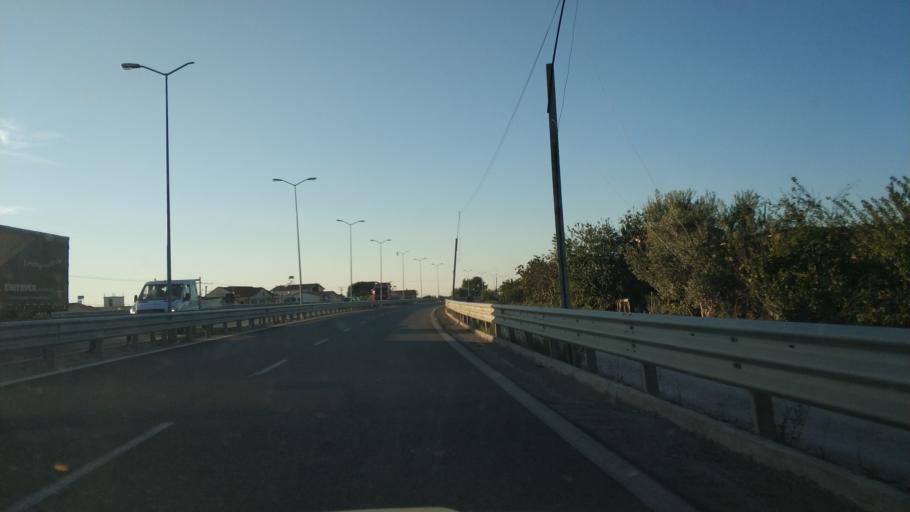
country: AL
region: Tirane
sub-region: Rrethi i Kavajes
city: Gose e Madhe
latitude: 41.0761
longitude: 19.6283
